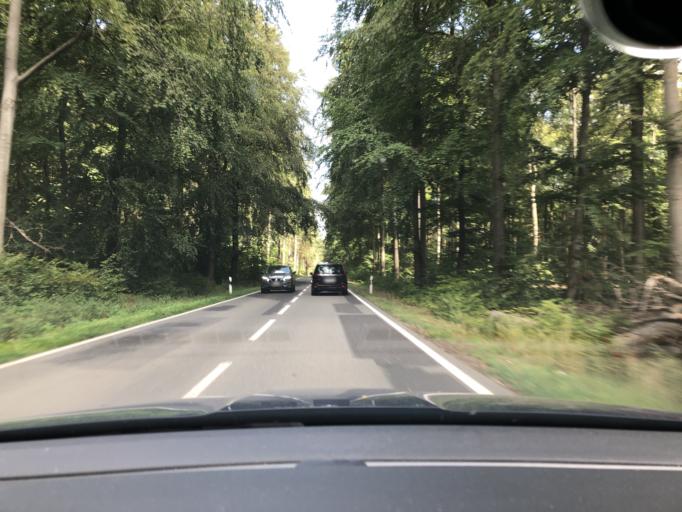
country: DE
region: Brandenburg
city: Neuruppin
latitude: 53.0247
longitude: 12.7438
